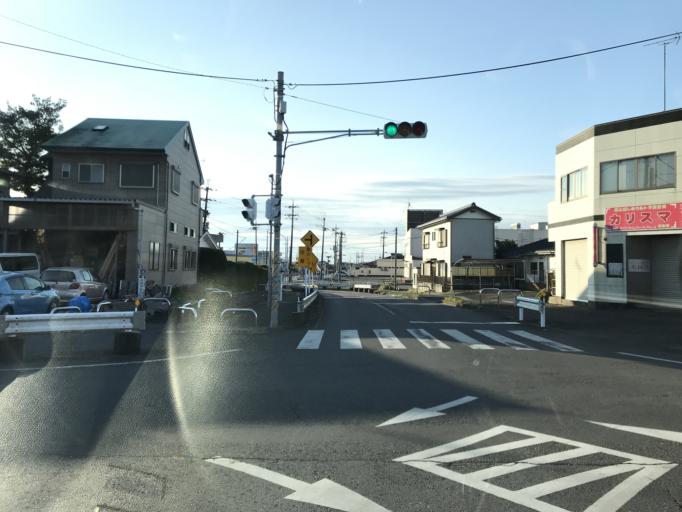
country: JP
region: Chiba
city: Yokaichiba
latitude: 35.7057
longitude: 140.5582
